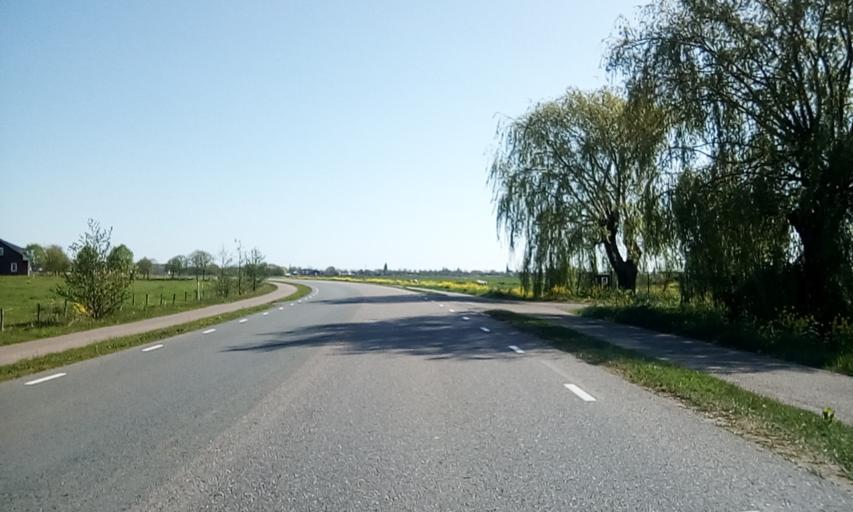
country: NL
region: Gelderland
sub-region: Gemeente Druten
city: Druten
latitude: 51.8763
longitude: 5.5610
